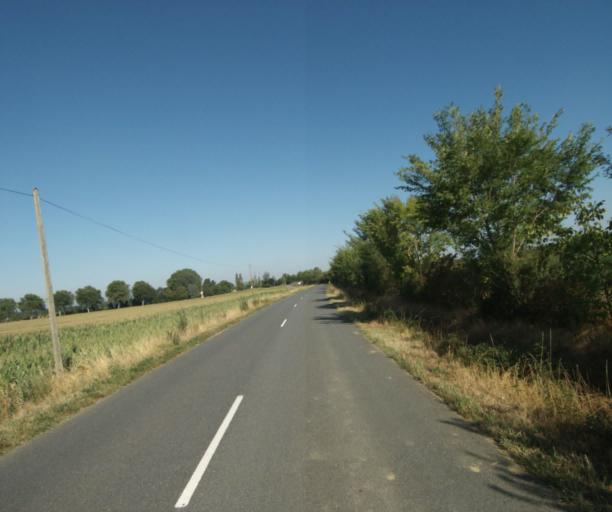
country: FR
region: Midi-Pyrenees
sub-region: Departement de la Haute-Garonne
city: Revel
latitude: 43.4741
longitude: 2.0195
